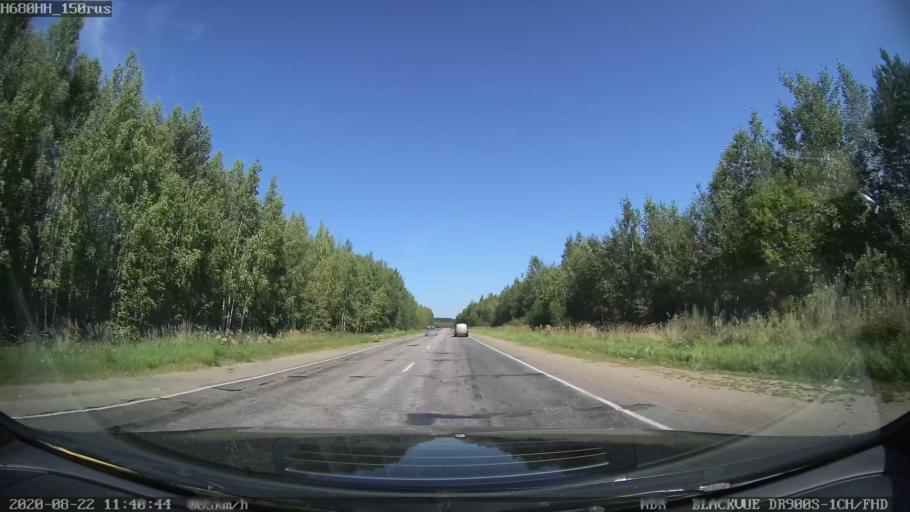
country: RU
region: Tverskaya
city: Sakharovo
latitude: 56.9806
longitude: 36.0236
